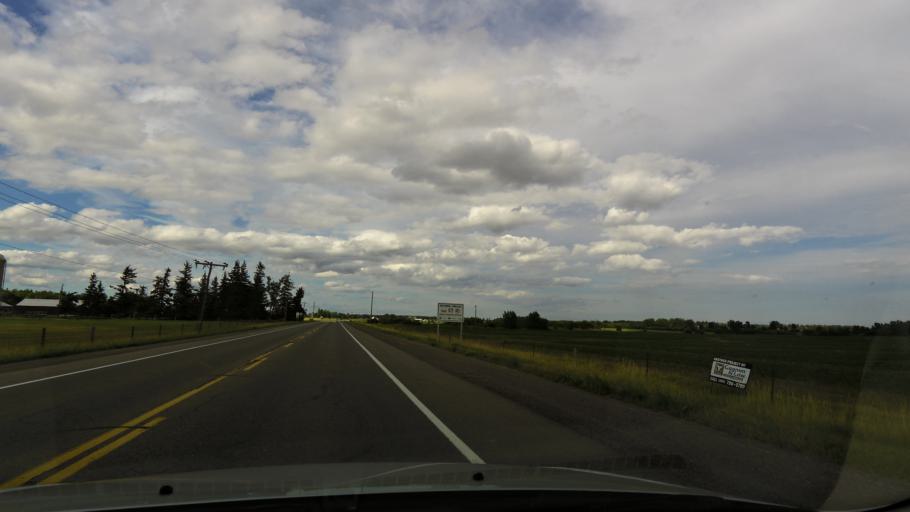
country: CA
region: Ontario
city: Brampton
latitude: 43.6755
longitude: -79.8882
